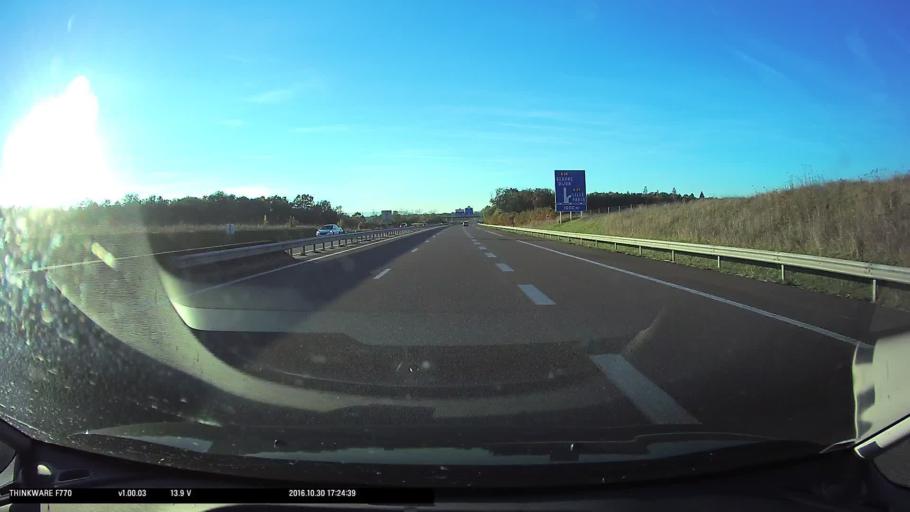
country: FR
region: Bourgogne
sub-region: Departement de la Cote-d'Or
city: Chevigny-Saint-Sauveur
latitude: 47.2699
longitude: 5.1639
